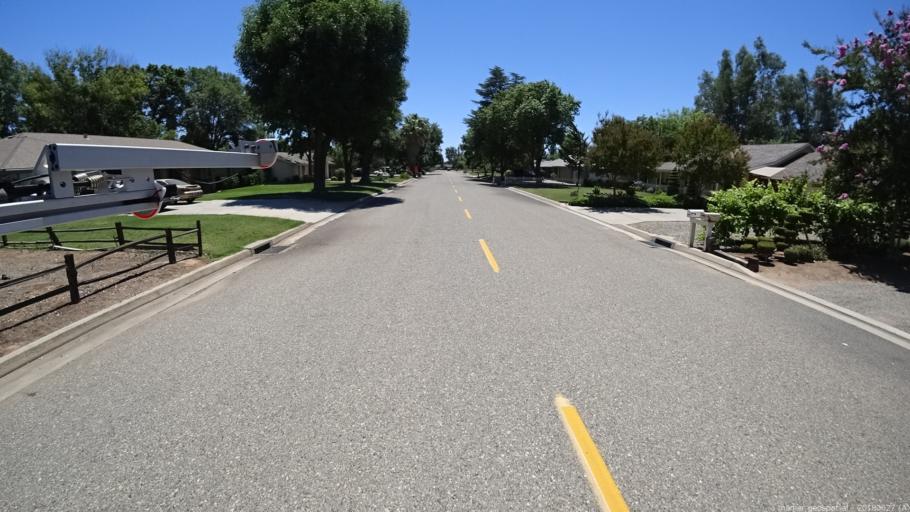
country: US
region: California
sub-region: Madera County
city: Bonadelle Ranchos-Madera Ranchos
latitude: 36.9254
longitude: -119.8927
